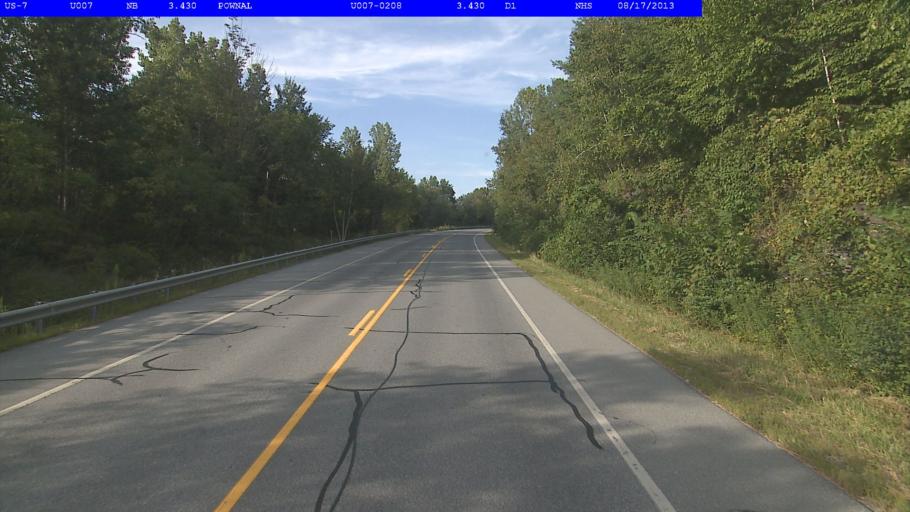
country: US
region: Massachusetts
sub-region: Berkshire County
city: Williamstown
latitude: 42.7843
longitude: -73.2422
